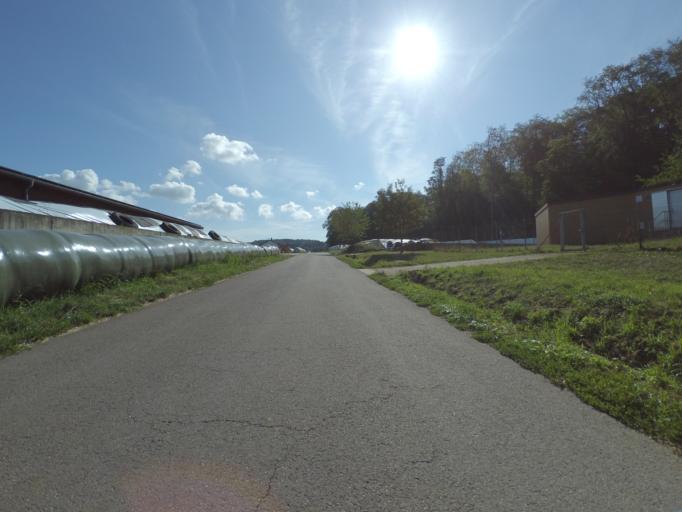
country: DE
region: Saarland
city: Perl
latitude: 49.5051
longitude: 6.3931
